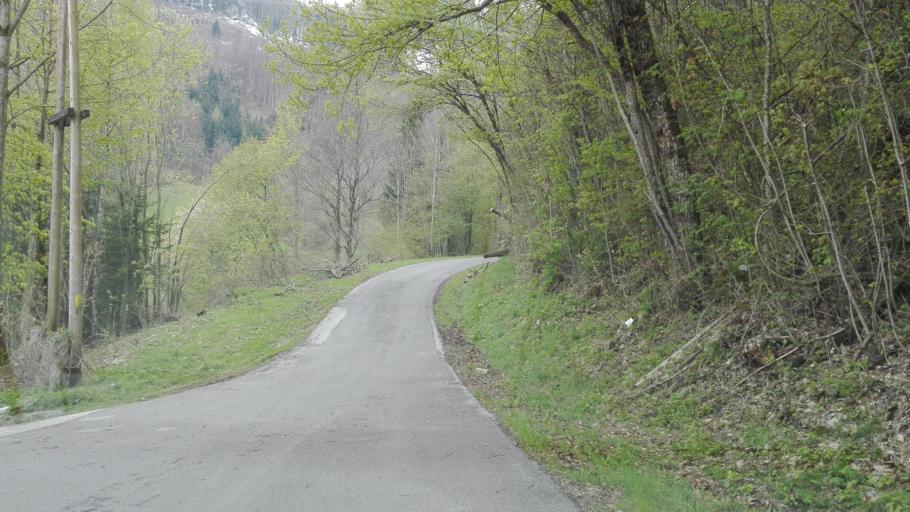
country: AT
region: Upper Austria
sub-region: Politischer Bezirk Steyr-Land
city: Ternberg
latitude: 47.9210
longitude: 14.3188
